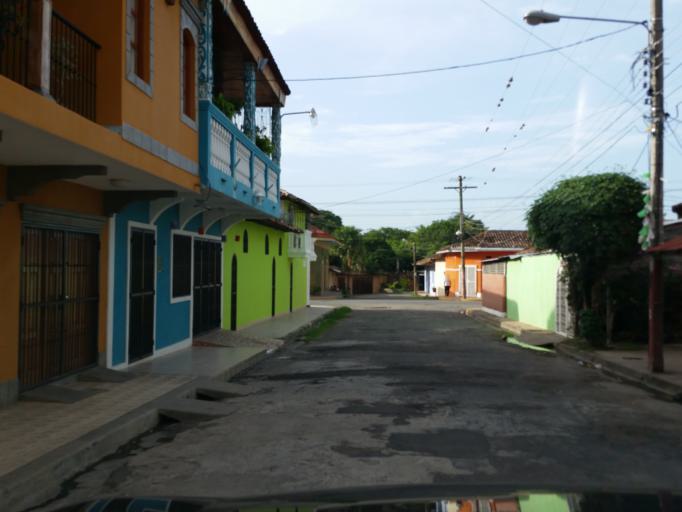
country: NI
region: Granada
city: Granada
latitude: 11.9337
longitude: -85.9505
